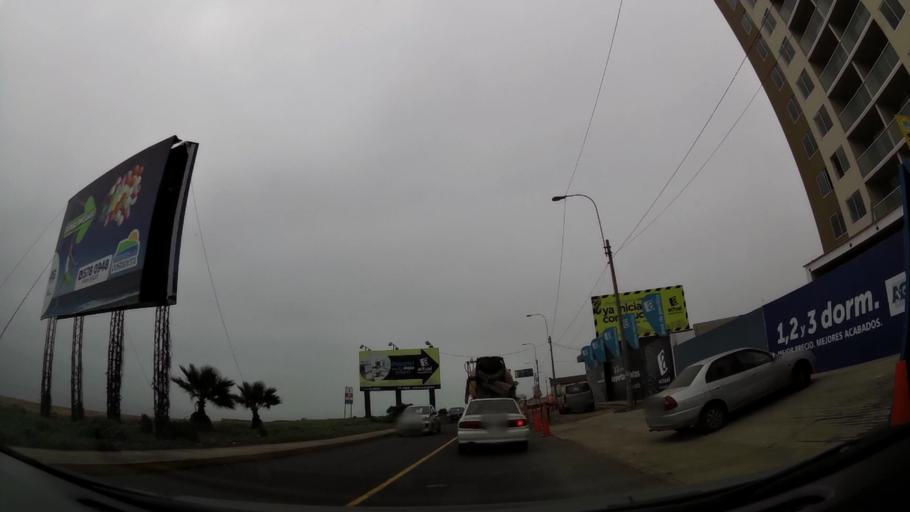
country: PE
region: Callao
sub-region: Callao
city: Callao
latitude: -12.0808
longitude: -77.1073
